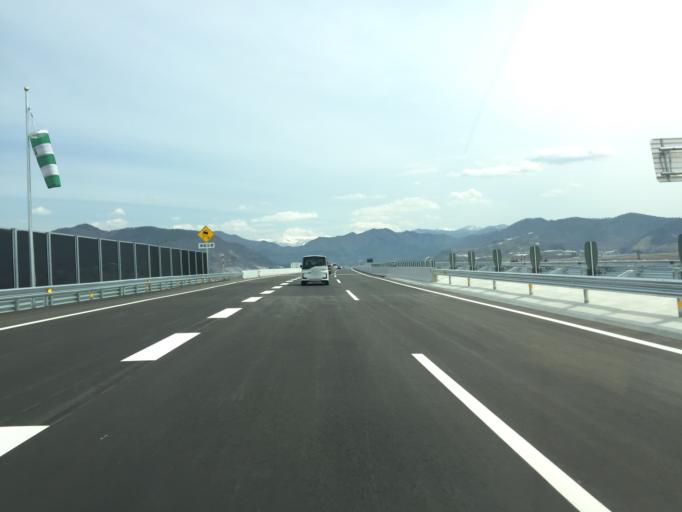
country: JP
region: Yamagata
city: Takahata
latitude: 38.0262
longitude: 140.1664
